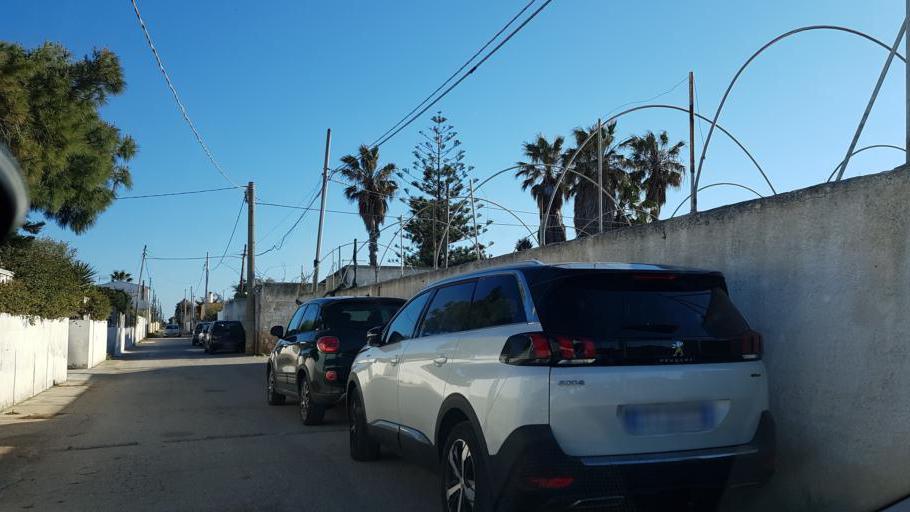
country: IT
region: Apulia
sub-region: Provincia di Brindisi
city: Materdomini
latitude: 40.6752
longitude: 17.9407
